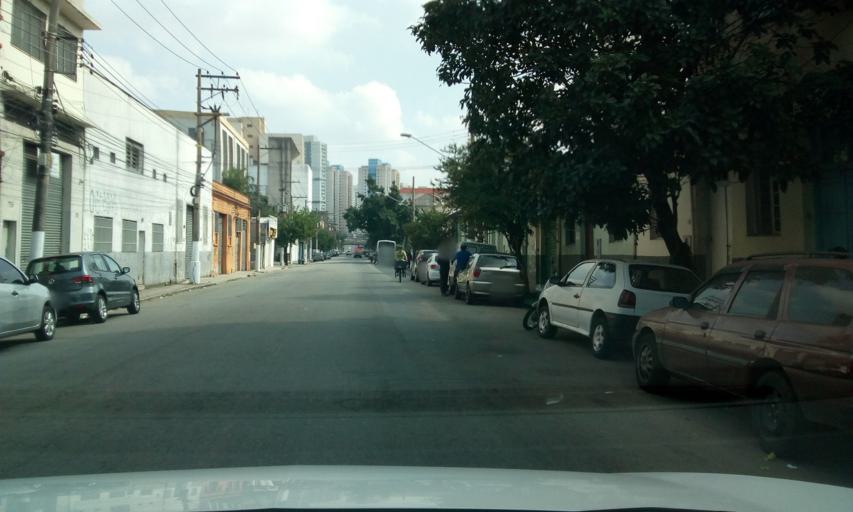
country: BR
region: Sao Paulo
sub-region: Sao Paulo
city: Sao Paulo
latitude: -23.5246
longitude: -46.6450
